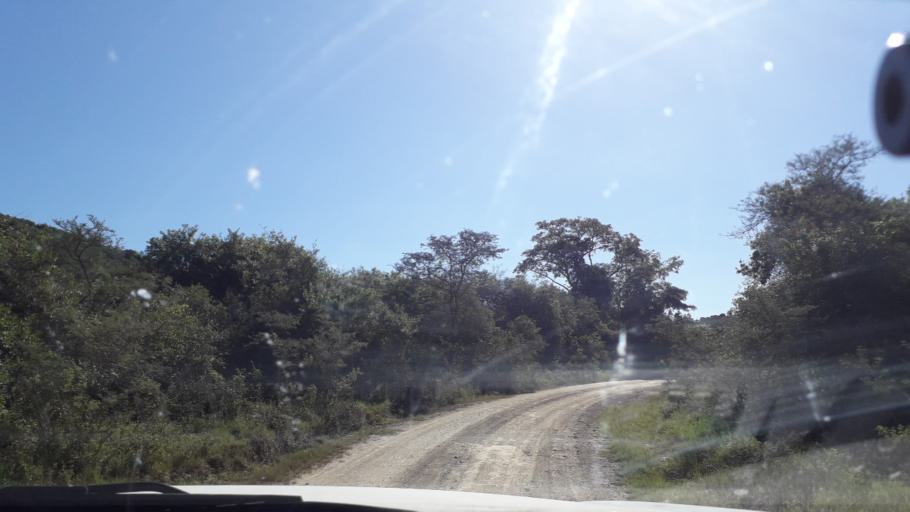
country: ZA
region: Eastern Cape
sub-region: Amathole District Municipality
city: Komga
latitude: -32.7665
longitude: 27.9619
